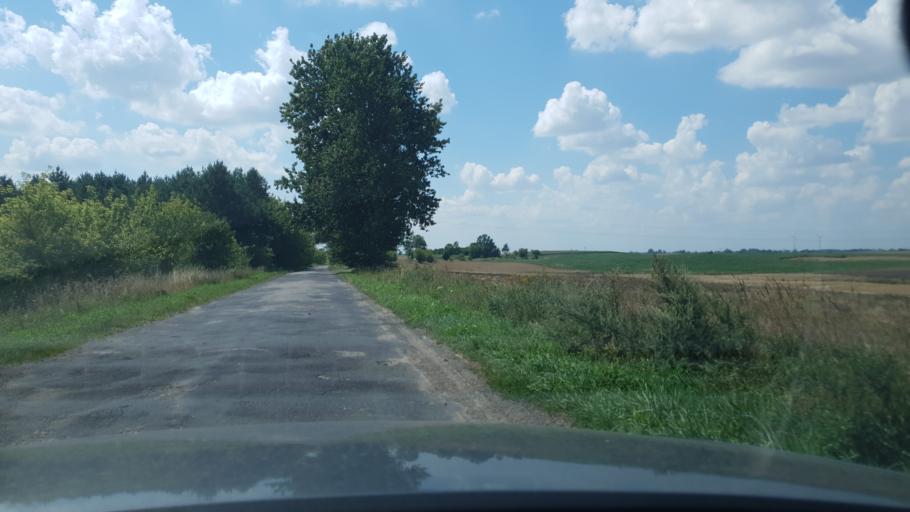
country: PL
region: Kujawsko-Pomorskie
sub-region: Powiat wabrzeski
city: Pluznica
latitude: 53.3066
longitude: 18.8146
